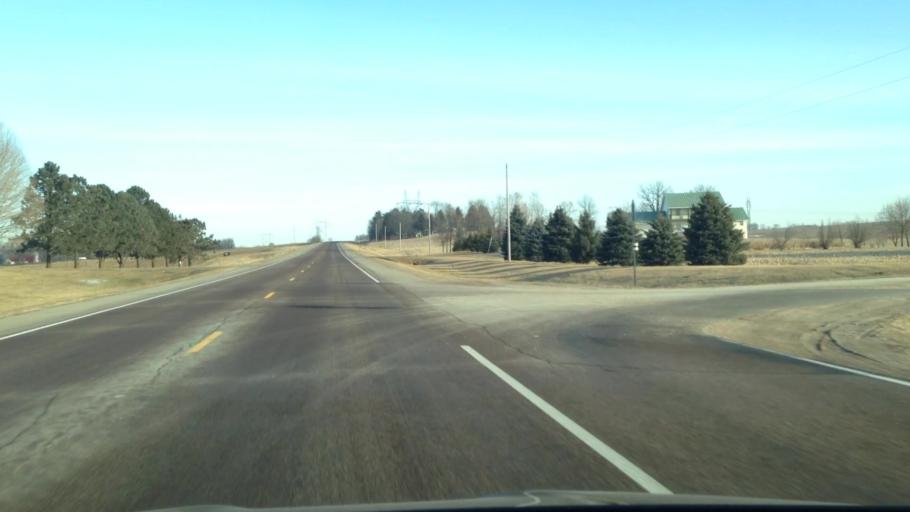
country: US
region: Minnesota
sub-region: Goodhue County
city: Zumbrota
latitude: 44.3066
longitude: -92.6644
